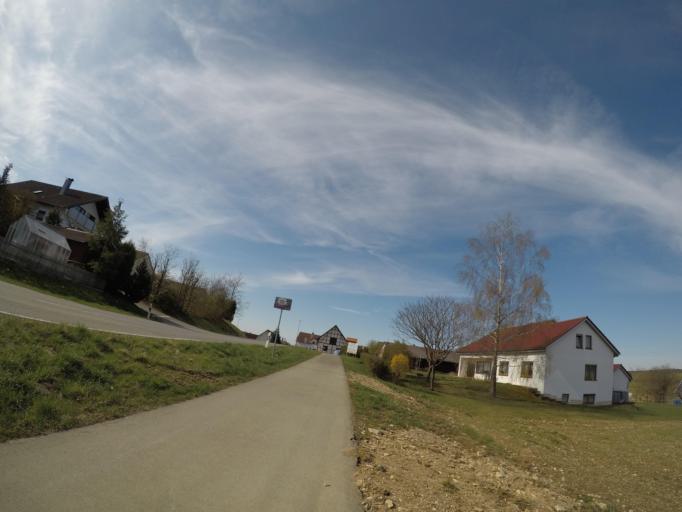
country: DE
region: Baden-Wuerttemberg
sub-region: Tuebingen Region
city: Mehrstetten
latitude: 48.3340
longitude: 9.6019
